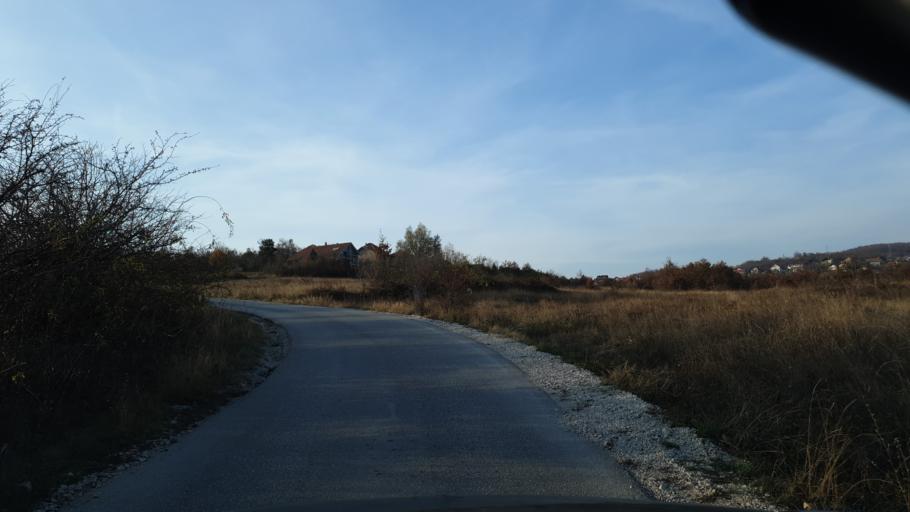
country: RS
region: Central Serbia
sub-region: Borski Okrug
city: Bor
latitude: 44.0508
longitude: 22.0912
